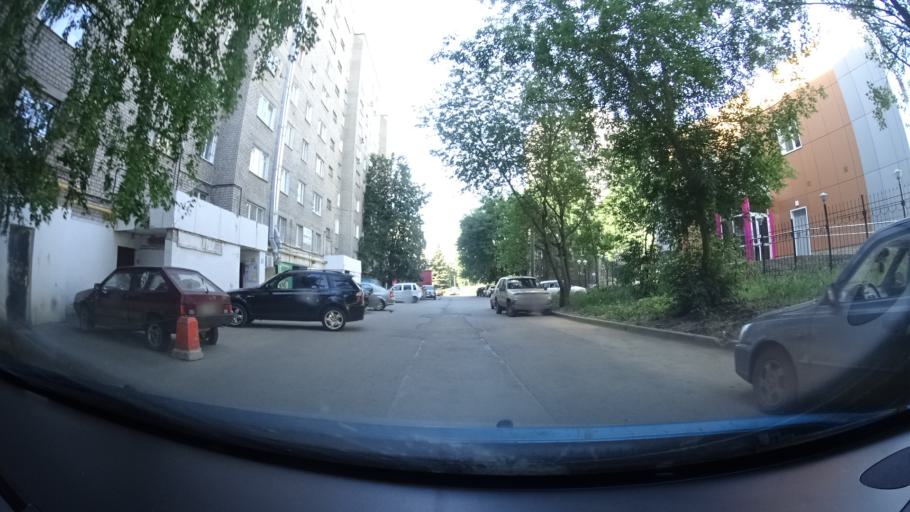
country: RU
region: Bashkortostan
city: Ufa
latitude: 54.7578
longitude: 55.9941
